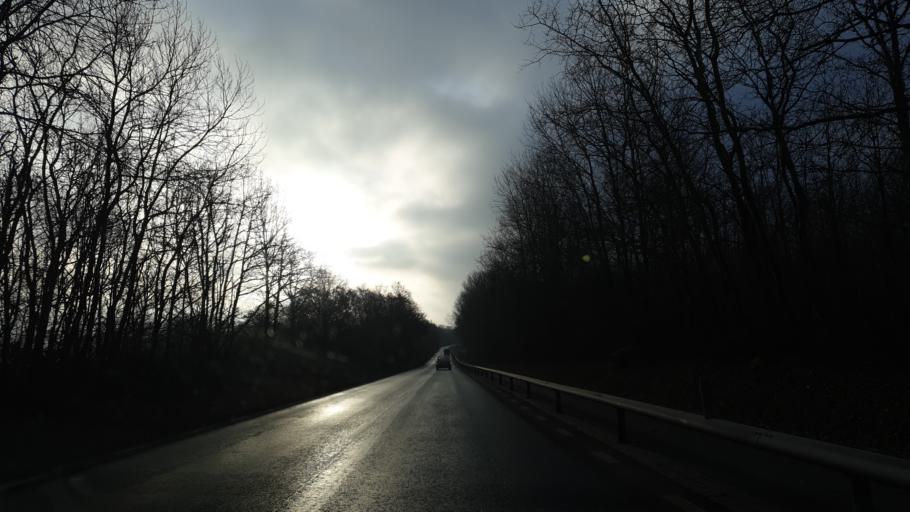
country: SE
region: Blekinge
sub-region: Karlshamns Kommun
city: Morrum
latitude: 56.1374
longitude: 14.6713
